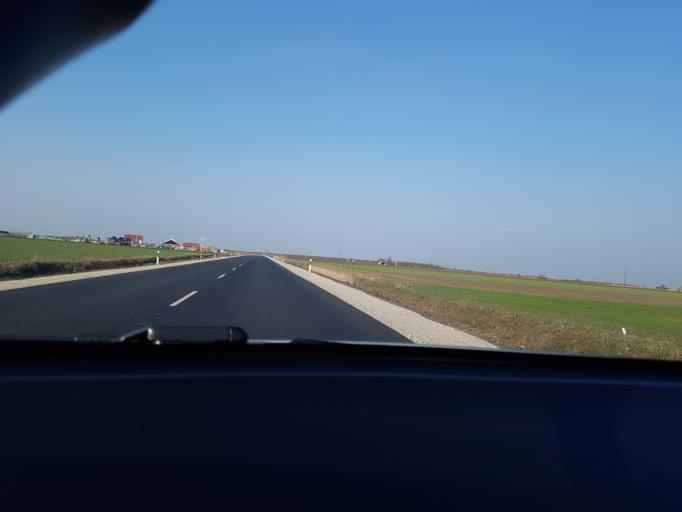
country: RO
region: Arad
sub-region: Comuna Nadlac
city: Nadlac
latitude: 46.2002
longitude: 20.7158
